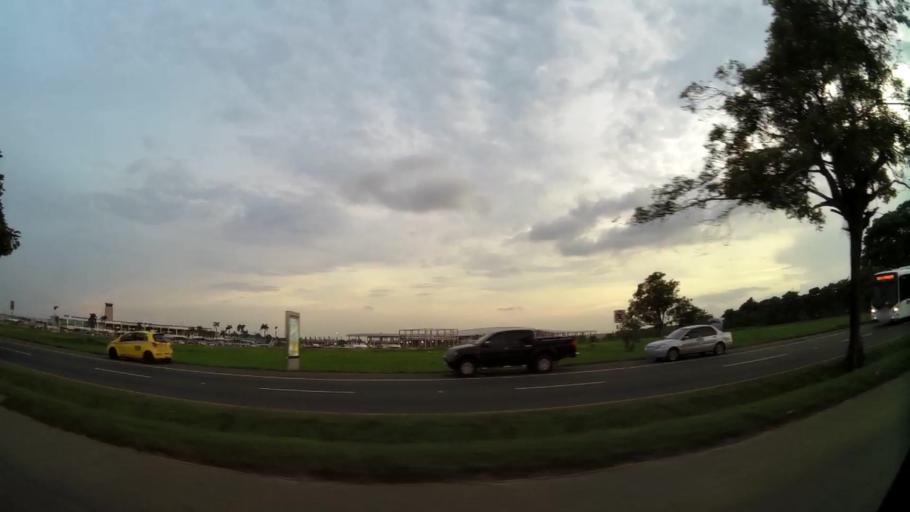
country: PA
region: Panama
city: Tocumen
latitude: 9.0700
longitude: -79.3913
